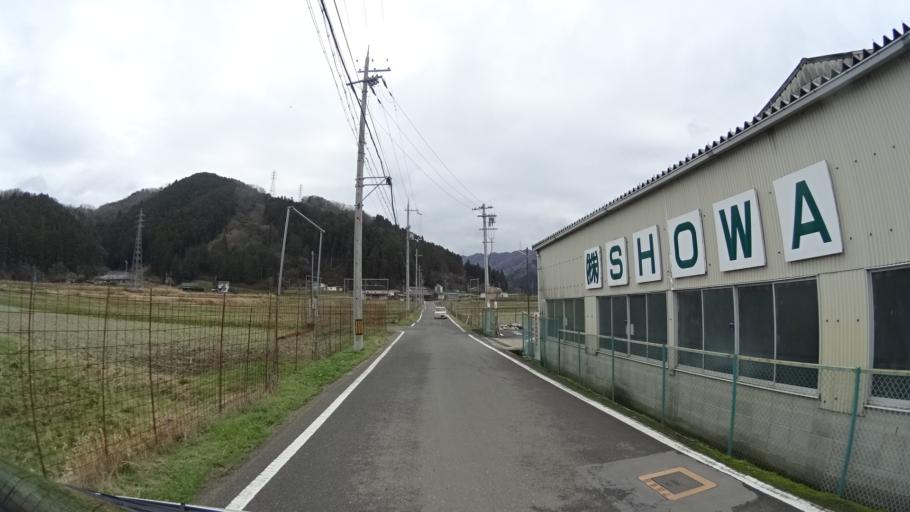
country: JP
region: Kyoto
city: Ayabe
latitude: 35.3345
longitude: 135.3483
